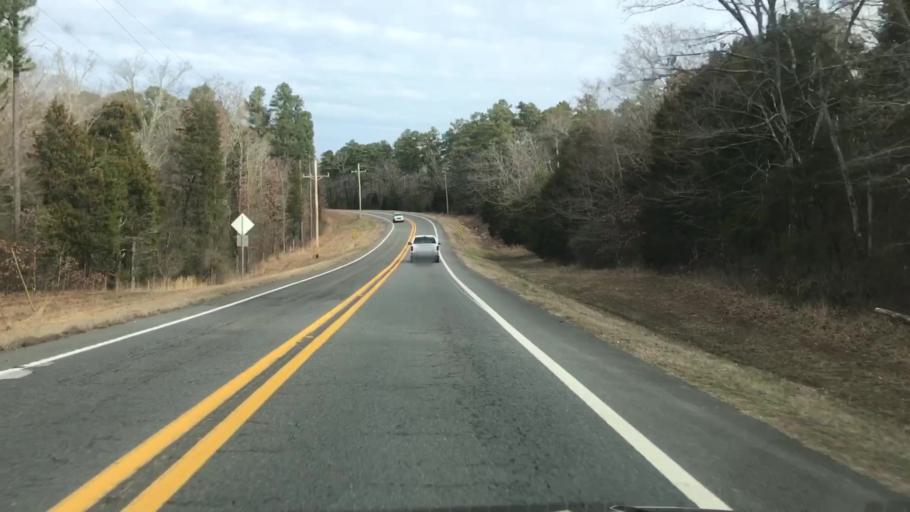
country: US
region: Arkansas
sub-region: Montgomery County
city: Mount Ida
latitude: 34.5862
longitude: -93.6634
